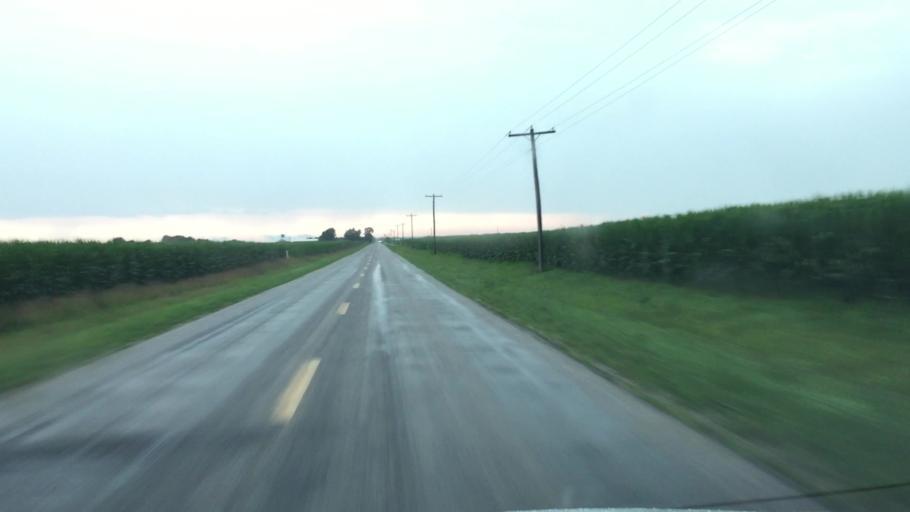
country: US
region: Iowa
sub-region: Lee County
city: Fort Madison
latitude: 40.5210
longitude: -91.2520
